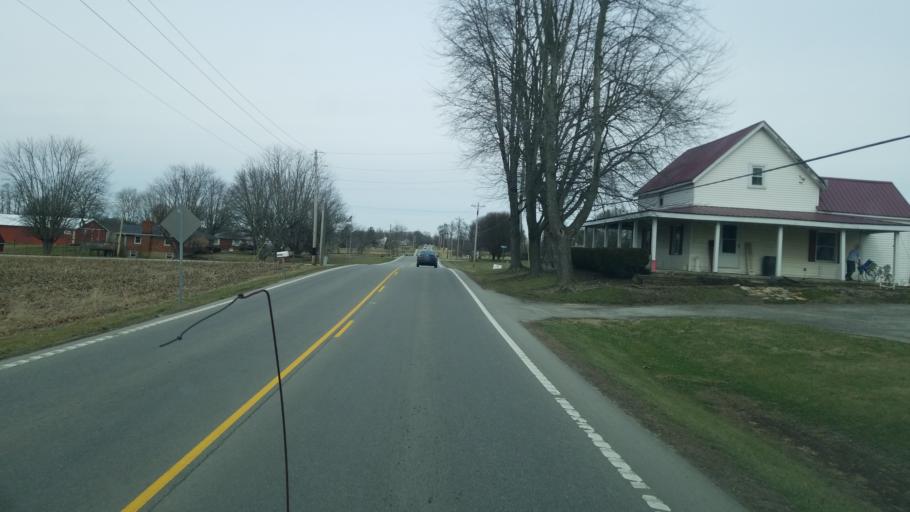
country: US
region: Ohio
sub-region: Highland County
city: Hillsboro
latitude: 39.1405
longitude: -83.6670
